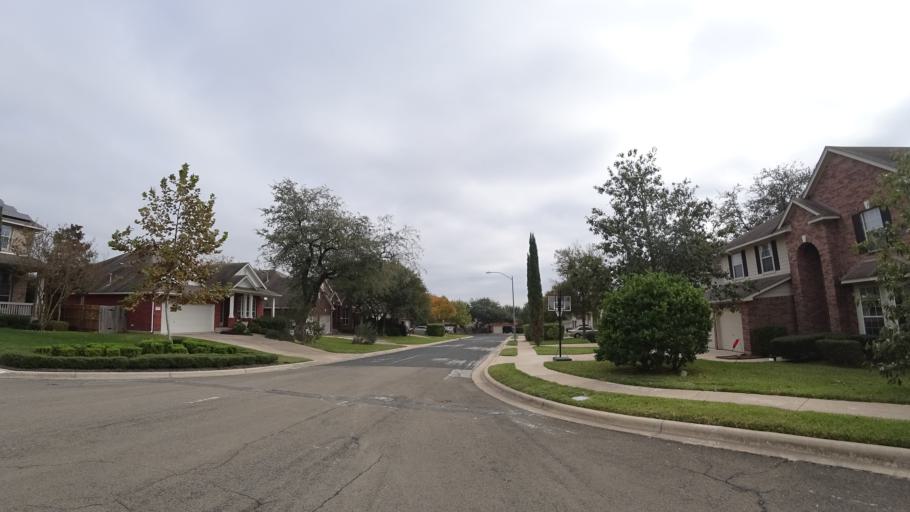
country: US
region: Texas
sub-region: Travis County
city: Barton Creek
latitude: 30.2267
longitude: -97.8785
